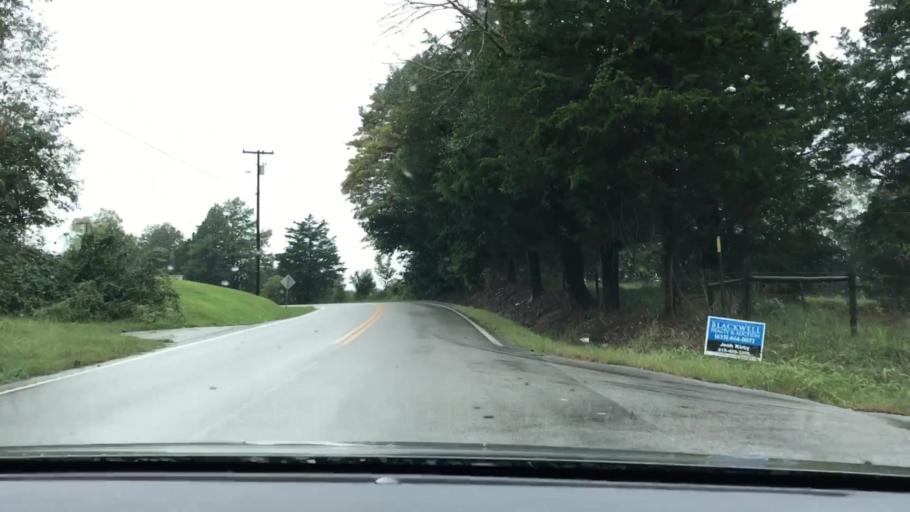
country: US
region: Tennessee
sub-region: Macon County
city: Red Boiling Springs
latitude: 36.4319
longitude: -85.8972
